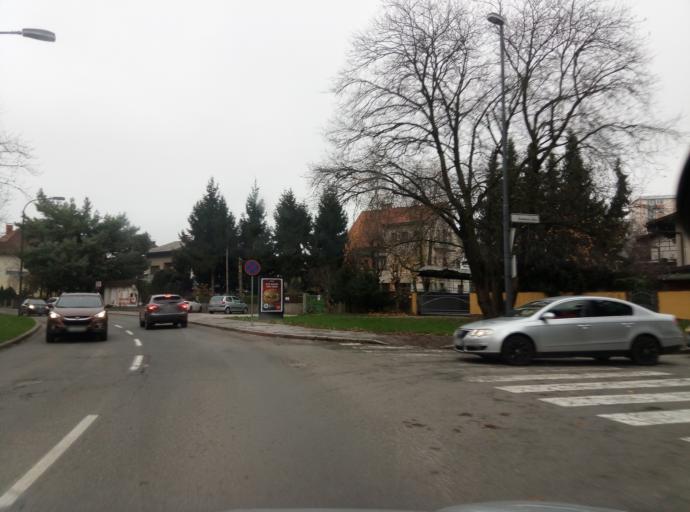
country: SI
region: Ljubljana
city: Ljubljana
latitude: 46.0737
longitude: 14.4839
